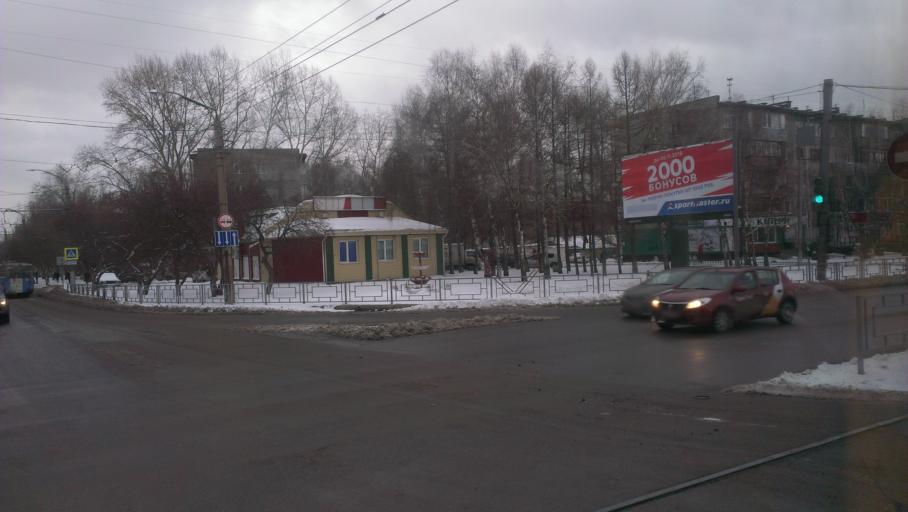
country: RU
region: Altai Krai
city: Novosilikatnyy
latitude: 53.3713
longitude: 83.6778
